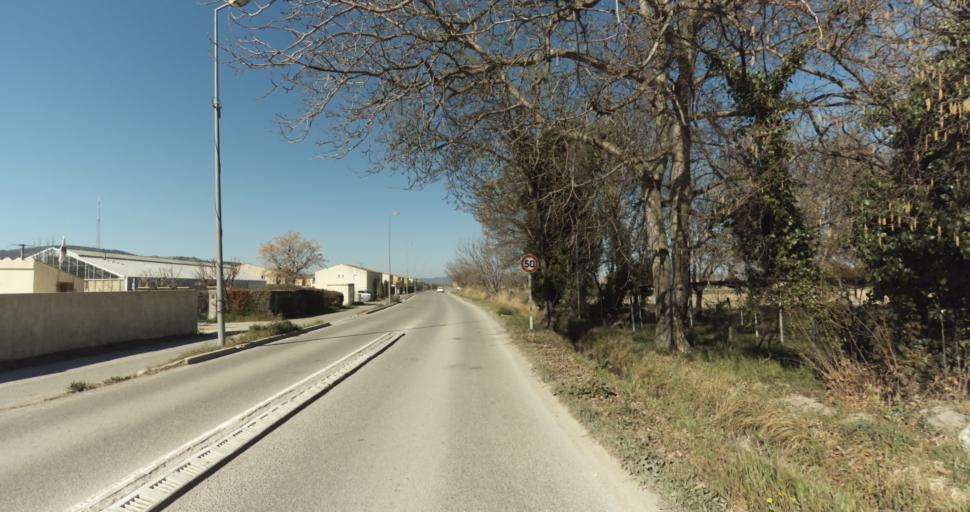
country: FR
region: Provence-Alpes-Cote d'Azur
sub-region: Departement des Bouches-du-Rhone
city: Peyrolles-en-Provence
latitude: 43.6489
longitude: 5.5808
